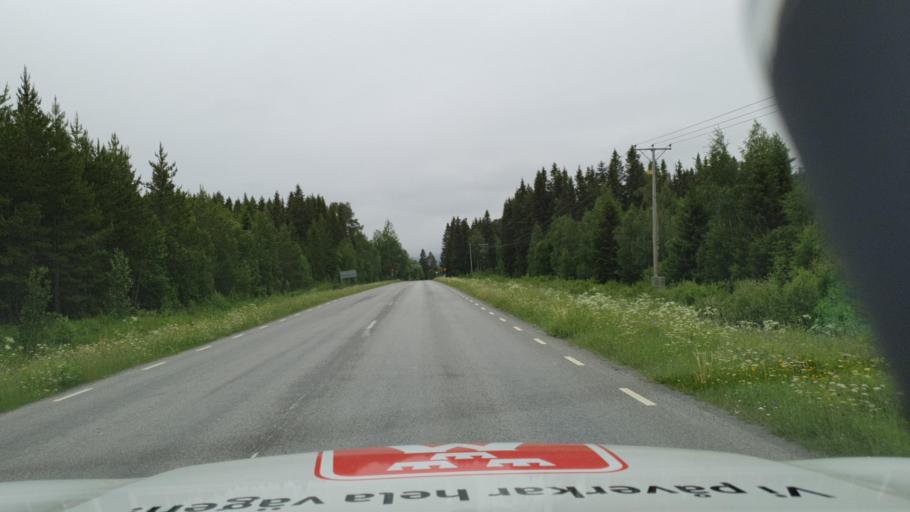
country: SE
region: Jaemtland
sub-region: Are Kommun
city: Jarpen
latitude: 63.3655
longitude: 13.4363
